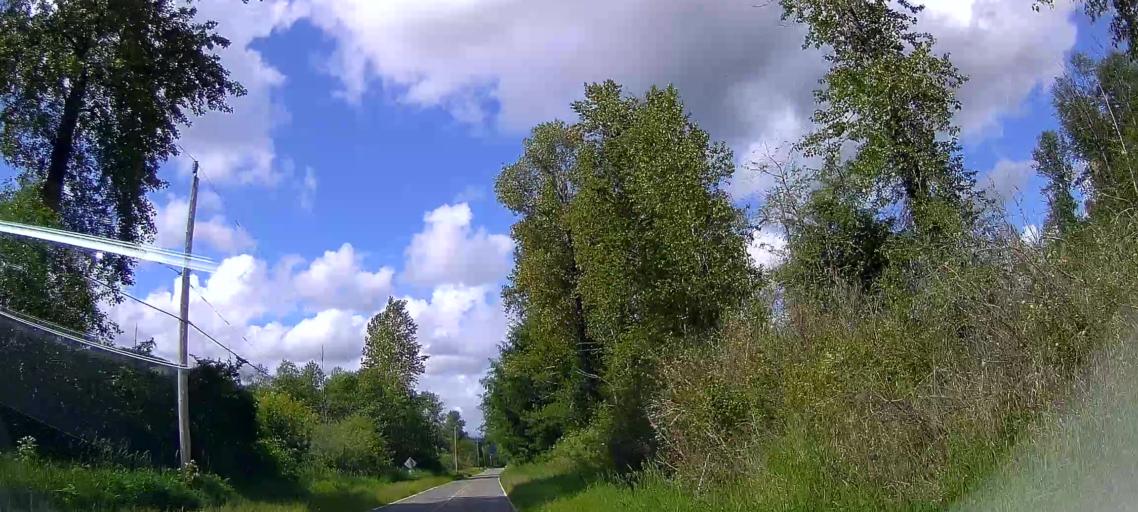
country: US
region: Washington
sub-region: Skagit County
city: Sedro-Woolley
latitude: 48.6537
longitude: -122.2042
